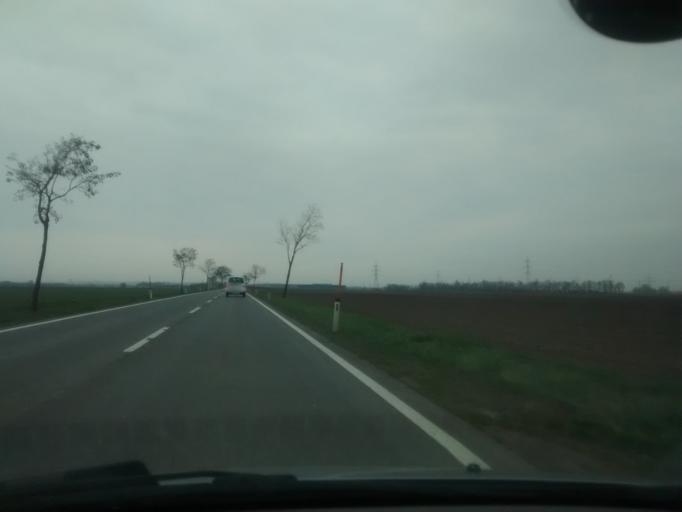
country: AT
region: Lower Austria
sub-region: Politischer Bezirk Modling
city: Achau
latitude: 48.0863
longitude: 16.3917
